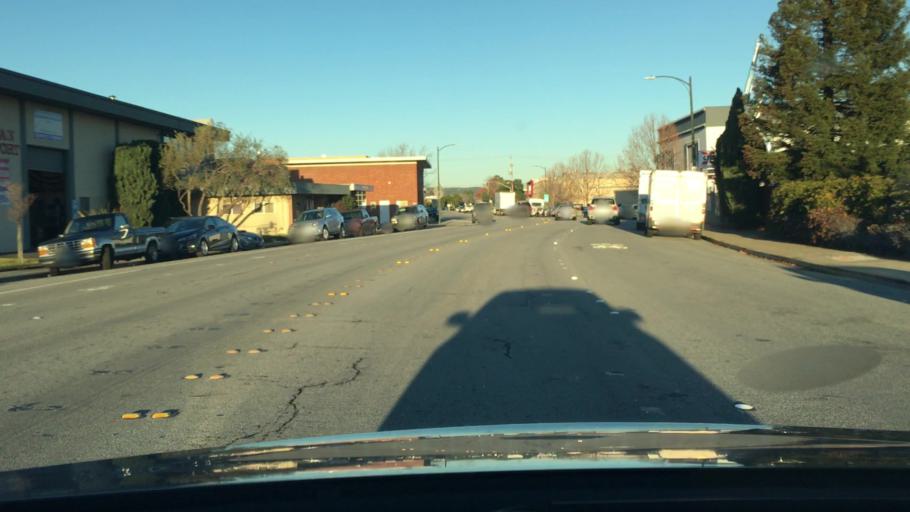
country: US
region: California
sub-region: San Mateo County
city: Burlingame
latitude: 37.5902
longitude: -122.3651
